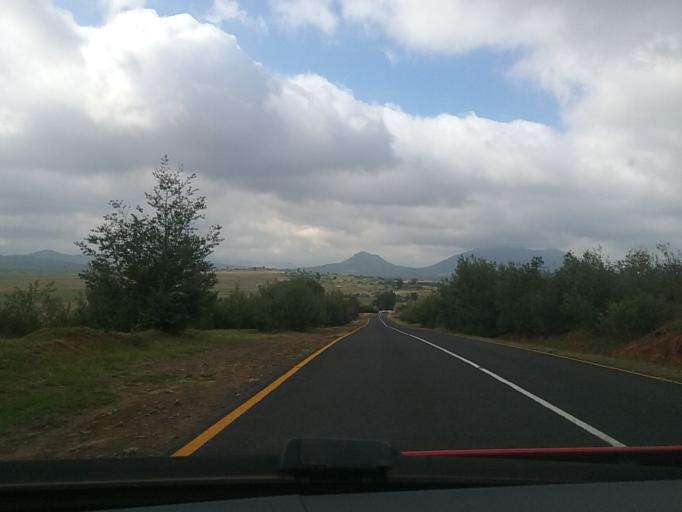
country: LS
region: Berea
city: Teyateyaneng
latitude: -29.1812
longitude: 27.7992
